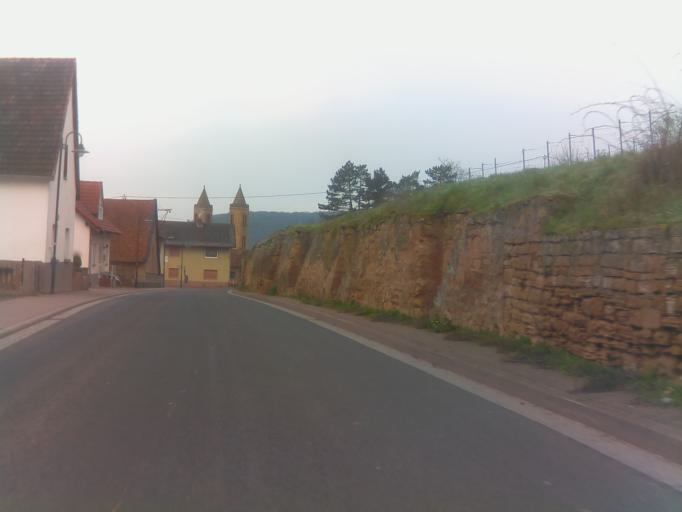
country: DE
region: Rheinland-Pfalz
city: Waldbockelheim
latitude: 49.8165
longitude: 7.7226
